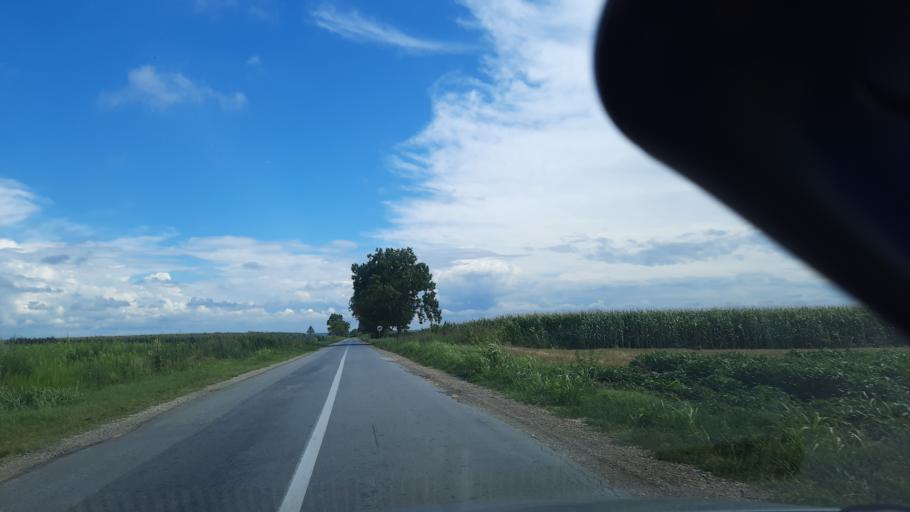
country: RS
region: Autonomna Pokrajina Vojvodina
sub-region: Sremski Okrug
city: Sremska Mitrovica
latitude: 45.0637
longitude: 19.5961
